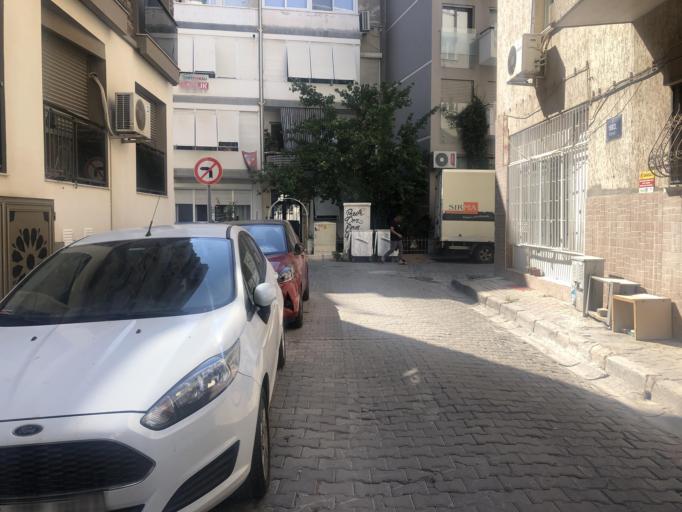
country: TR
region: Izmir
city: Karsiyaka
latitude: 38.4589
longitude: 27.1223
